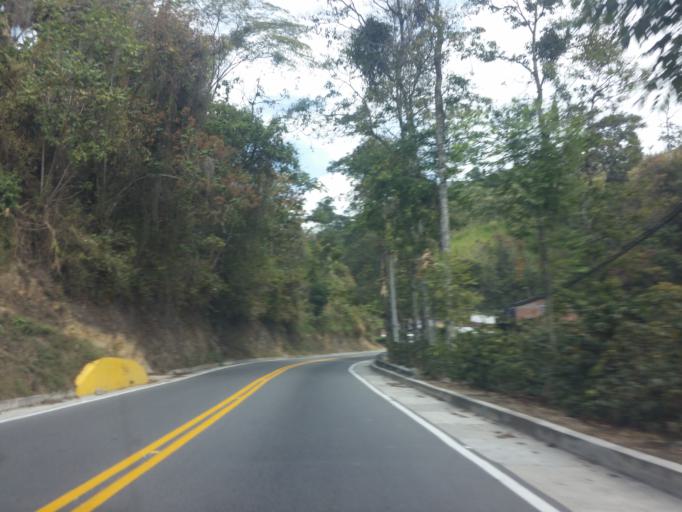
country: CO
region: Caldas
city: Villamaria
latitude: 5.0108
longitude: -75.5491
